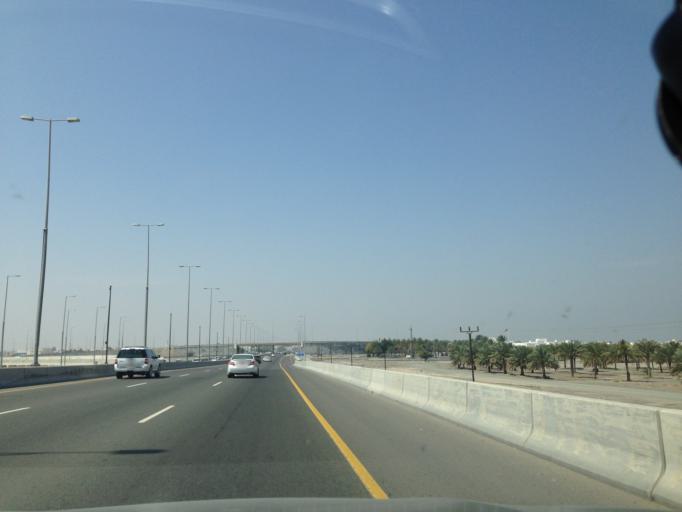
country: OM
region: Muhafazat Masqat
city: As Sib al Jadidah
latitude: 23.6642
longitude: 58.1659
